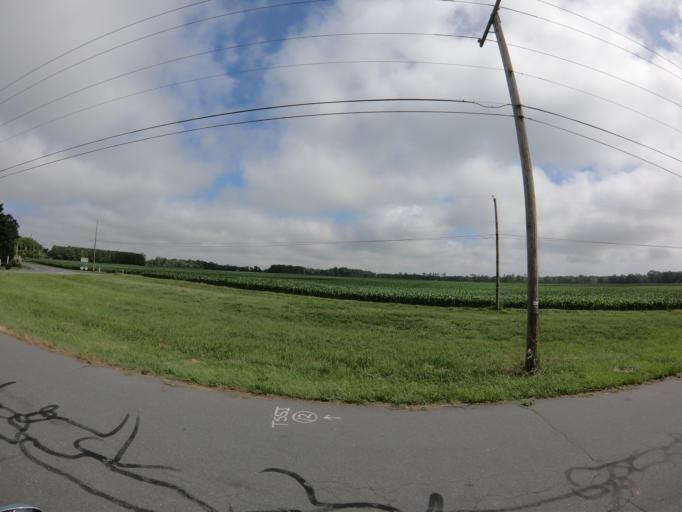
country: US
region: Delaware
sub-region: Kent County
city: Riverview
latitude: 39.0123
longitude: -75.4916
